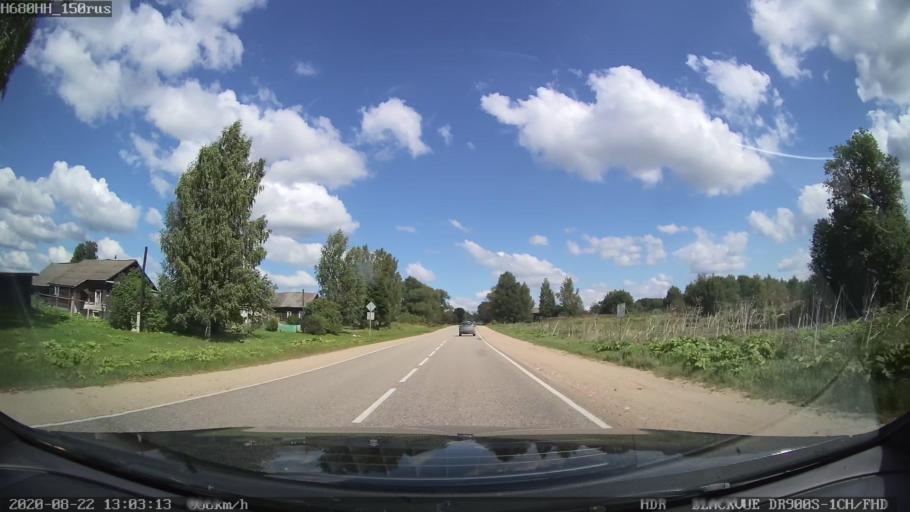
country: RU
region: Tverskaya
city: Bezhetsk
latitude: 57.6582
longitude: 36.4082
